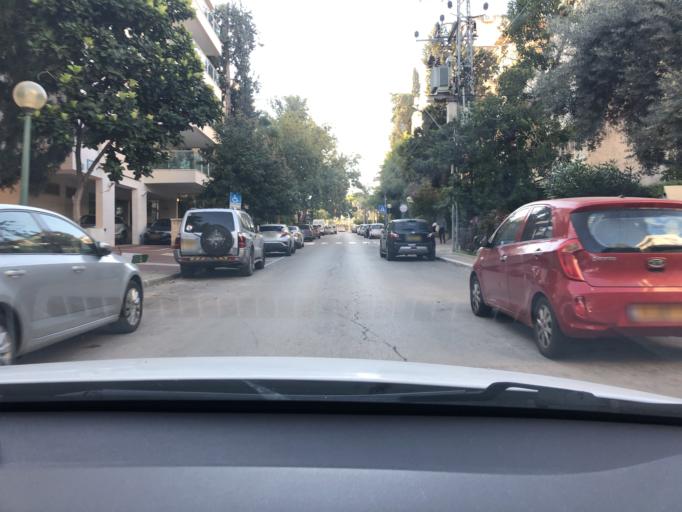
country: IL
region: Central District
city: Kfar Saba
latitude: 32.1719
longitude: 34.9033
